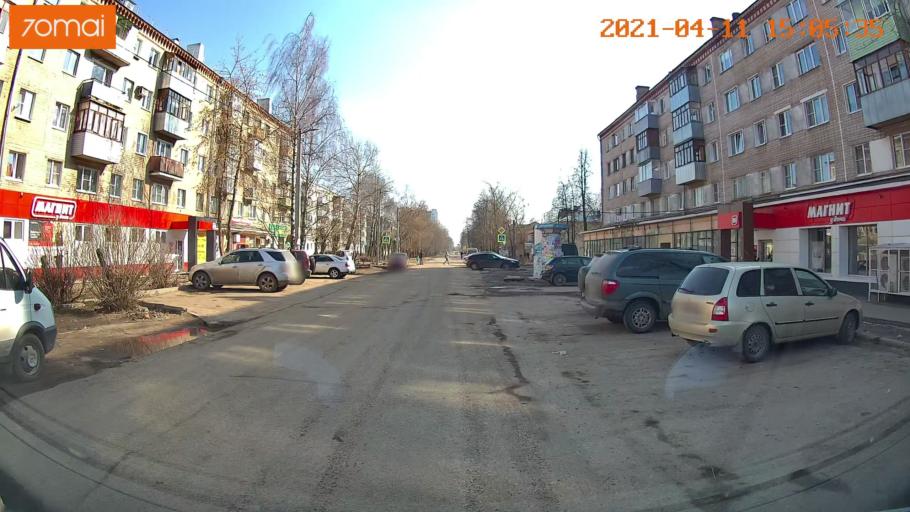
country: RU
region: Ivanovo
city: Bogorodskoye
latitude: 57.0220
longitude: 41.0150
